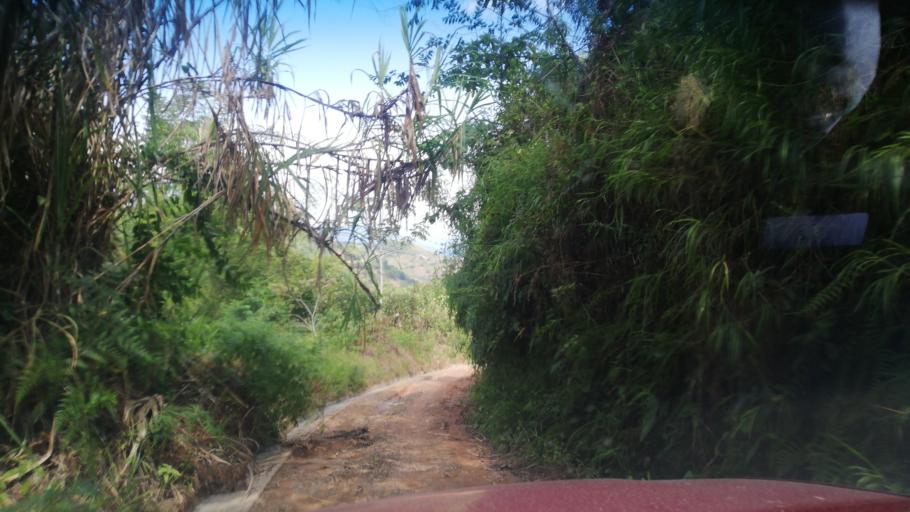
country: CO
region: Risaralda
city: Balboa
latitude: 4.9210
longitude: -75.9556
